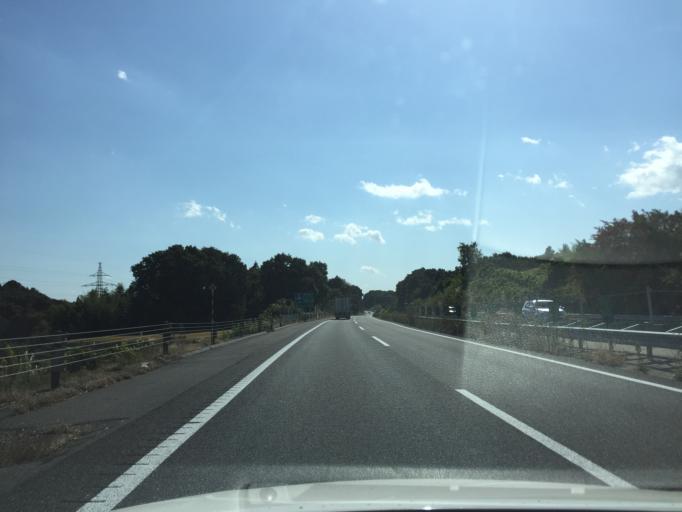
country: JP
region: Fukushima
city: Sukagawa
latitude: 37.3187
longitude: 140.3430
